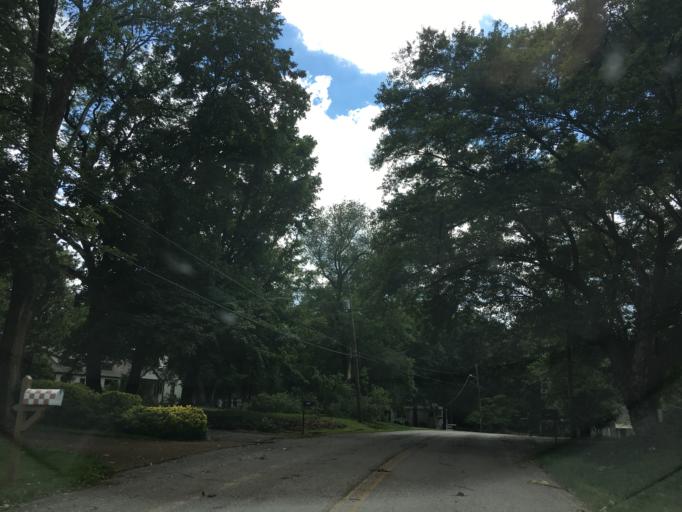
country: US
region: Tennessee
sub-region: Davidson County
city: Oak Hill
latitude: 36.0975
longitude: -86.7855
